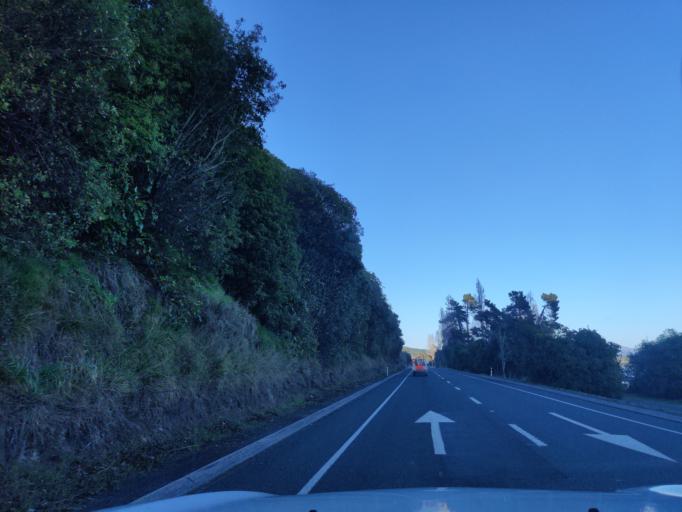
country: NZ
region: Waikato
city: Turangi
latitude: -38.8913
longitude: 175.9501
